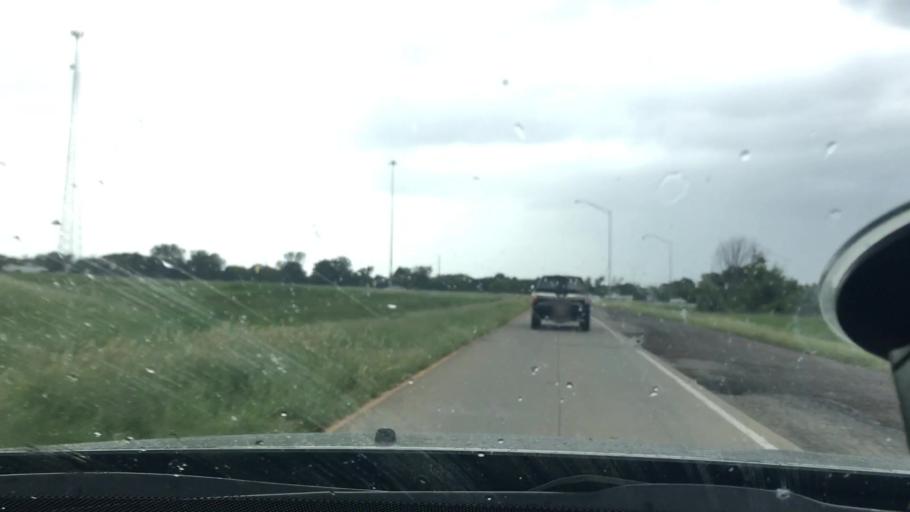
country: US
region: Oklahoma
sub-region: Okmulgee County
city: Henryetta
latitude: 35.4338
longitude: -95.9732
